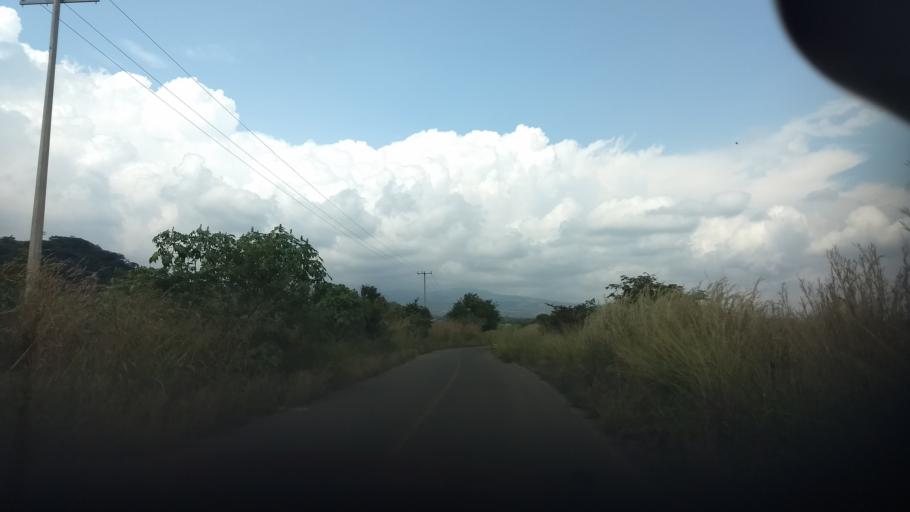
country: MX
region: Jalisco
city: Tonila
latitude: 19.4140
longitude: -103.4877
